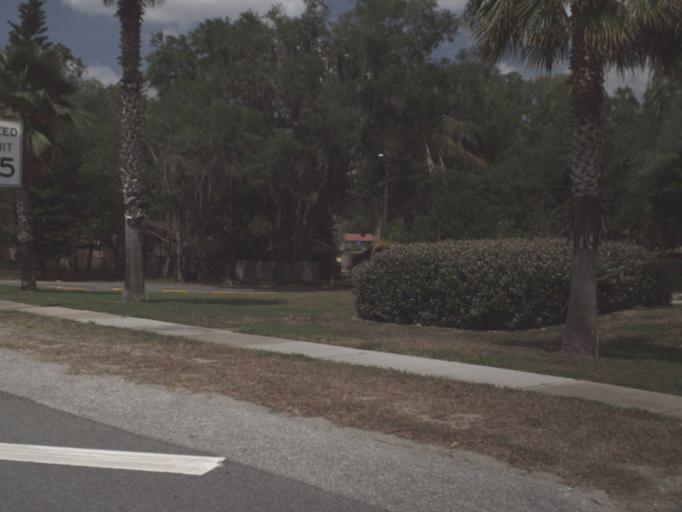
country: US
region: Florida
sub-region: Lake County
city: Mascotte
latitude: 28.5786
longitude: -81.8872
